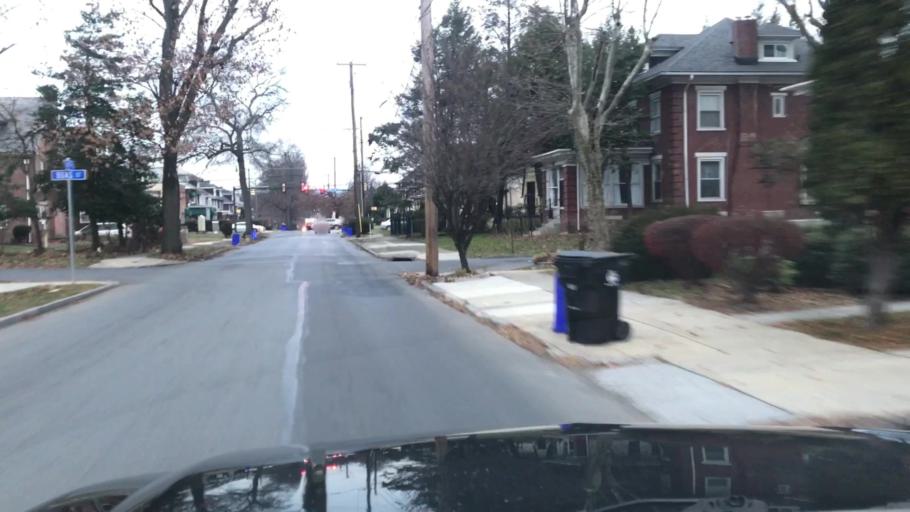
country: US
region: Pennsylvania
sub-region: Dauphin County
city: Harrisburg
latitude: 40.2747
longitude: -76.8683
